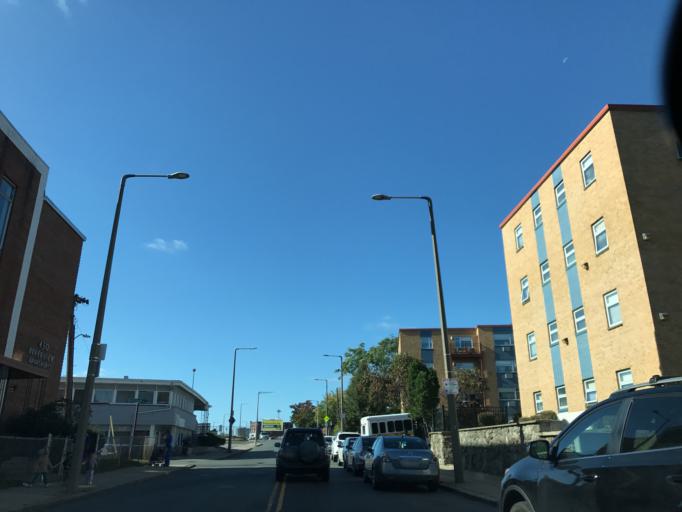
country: US
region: Massachusetts
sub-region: Norfolk County
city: Milton
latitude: 42.2694
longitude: -71.0910
